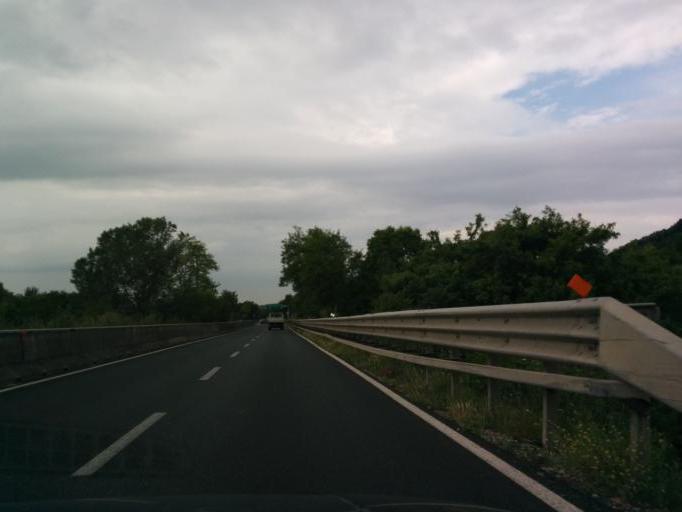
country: IT
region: Tuscany
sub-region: Province of Florence
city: San Casciano in Val di Pesa
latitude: 43.6218
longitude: 11.1854
